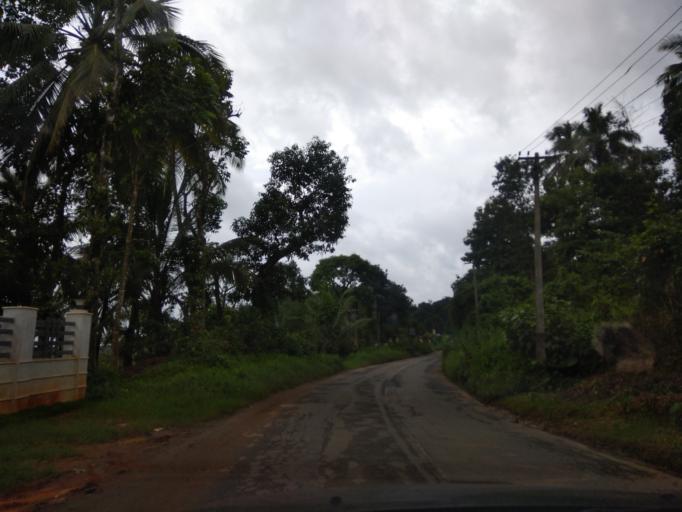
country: IN
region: Kerala
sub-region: Wayanad
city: Panamaram
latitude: 11.8220
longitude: 76.0204
